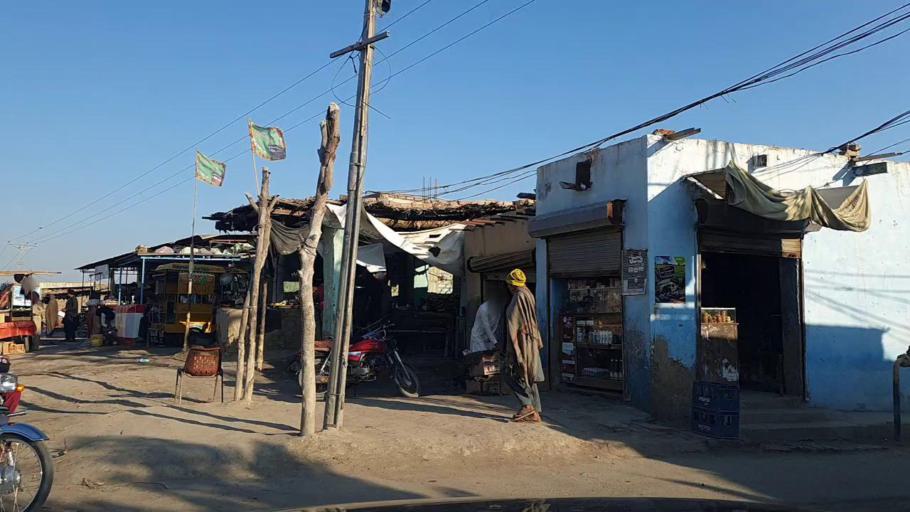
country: PK
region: Sindh
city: Nawabshah
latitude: 26.2270
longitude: 68.3613
